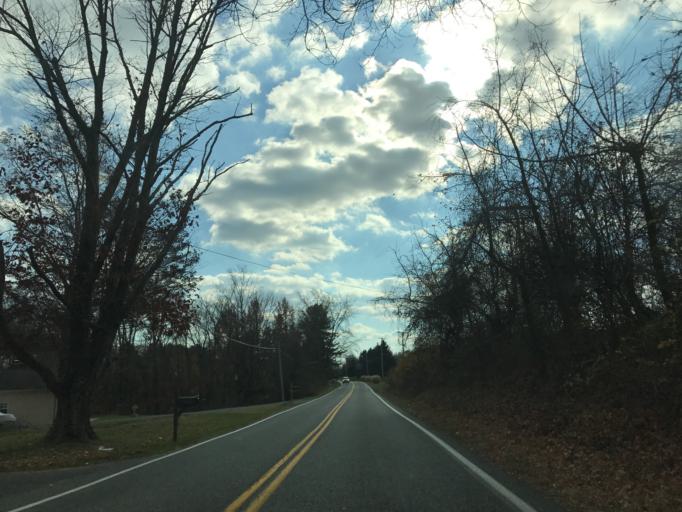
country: US
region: Maryland
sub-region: Harford County
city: Pleasant Hills
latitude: 39.4863
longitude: -76.3743
